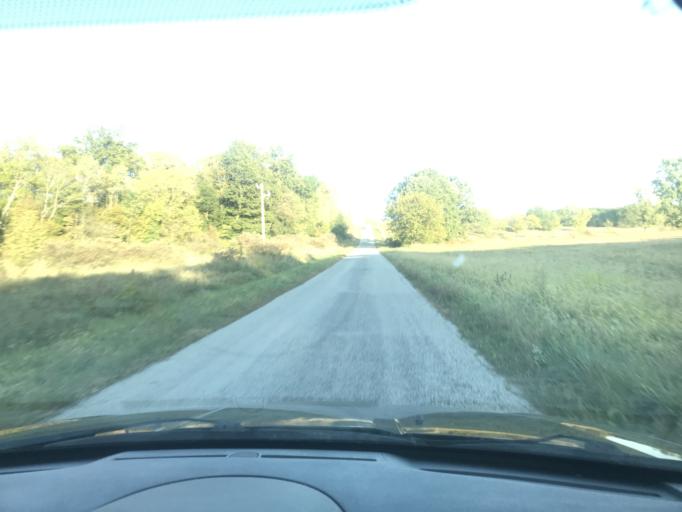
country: US
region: Ohio
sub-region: Logan County
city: De Graff
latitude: 40.2351
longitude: -83.8620
